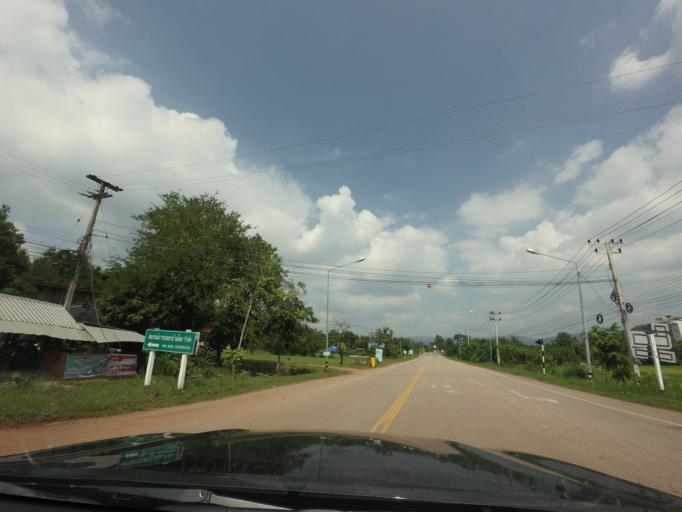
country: TH
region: Uttaradit
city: Ban Khok
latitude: 18.0274
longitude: 101.0748
